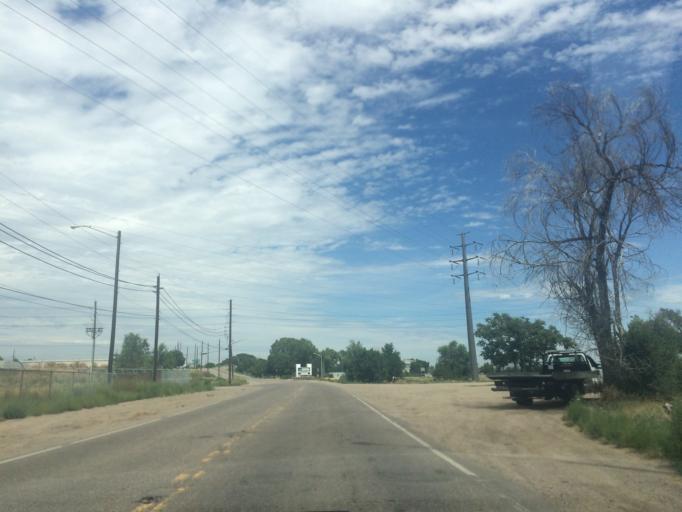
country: US
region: Colorado
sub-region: Adams County
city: Welby
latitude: 39.8118
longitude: -104.9596
